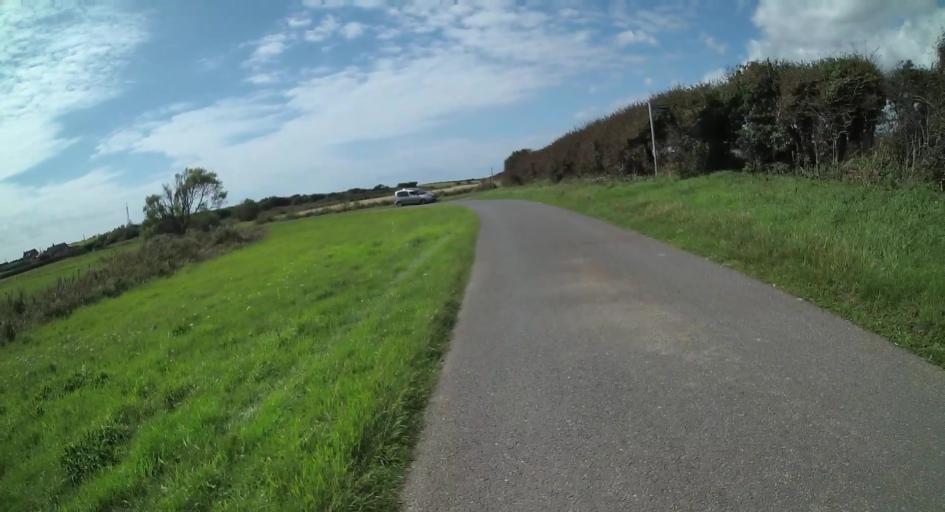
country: GB
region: England
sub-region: Isle of Wight
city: Chale
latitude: 50.6360
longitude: -1.3778
